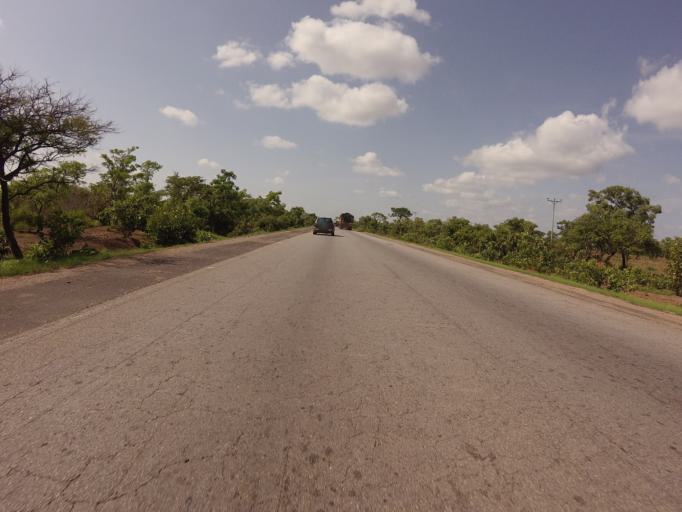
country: GH
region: Northern
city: Savelugu
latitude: 9.9530
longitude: -0.8357
